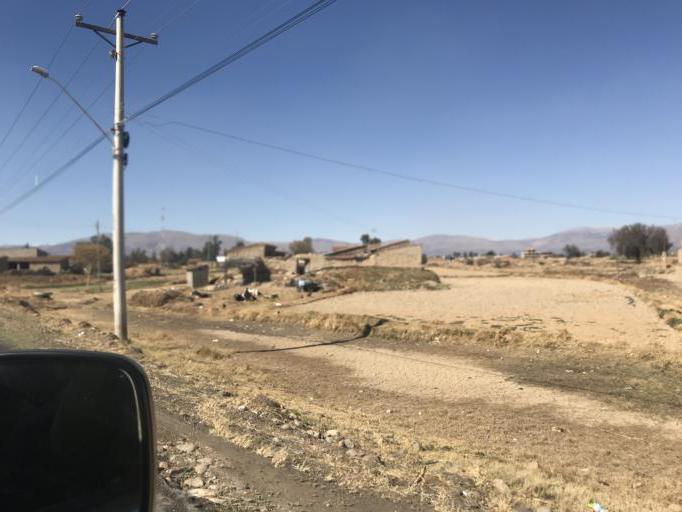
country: BO
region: Cochabamba
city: Cliza
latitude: -17.5674
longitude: -65.8923
